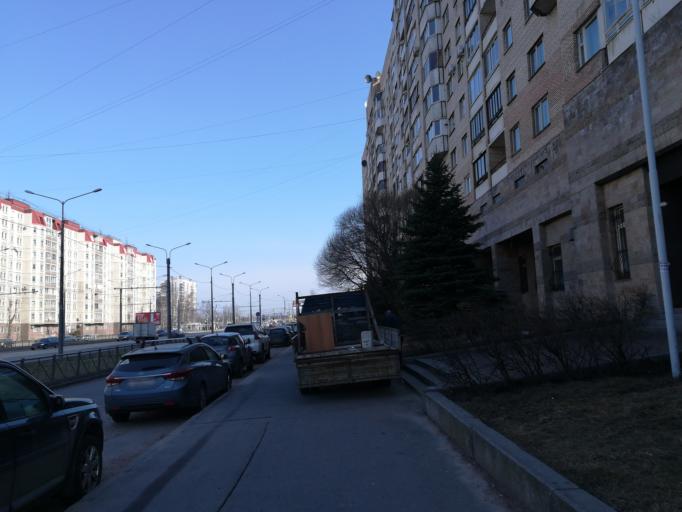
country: RU
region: St.-Petersburg
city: Vasyl'evsky Ostrov
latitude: 59.9527
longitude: 30.2350
